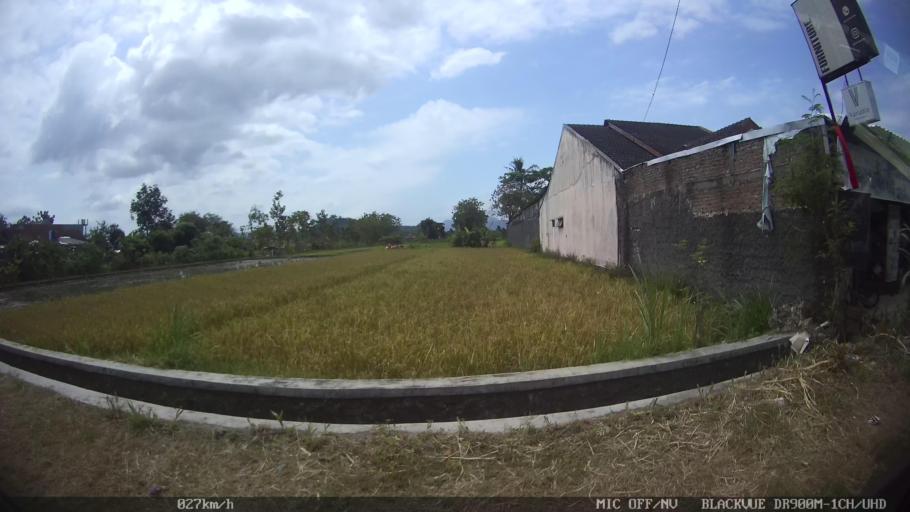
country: ID
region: Daerah Istimewa Yogyakarta
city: Depok
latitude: -7.8249
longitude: 110.4425
